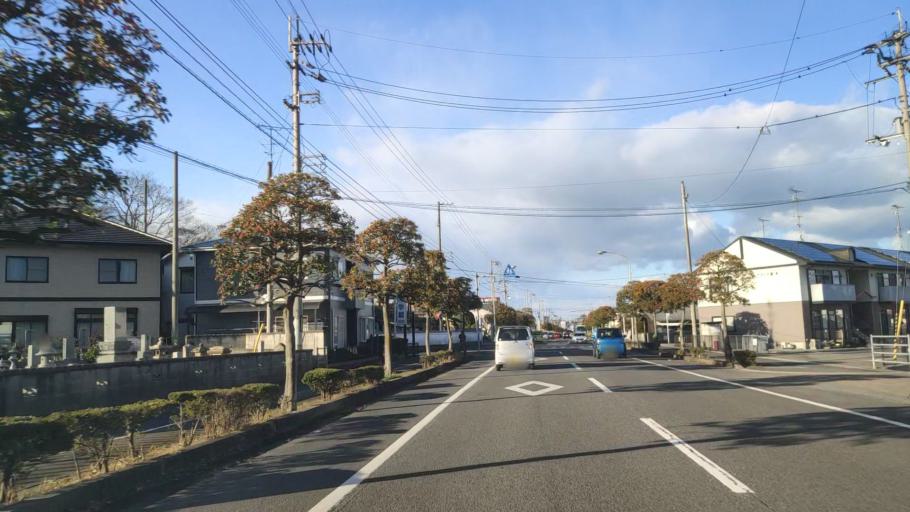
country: JP
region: Ehime
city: Saijo
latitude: 33.9226
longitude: 133.1842
